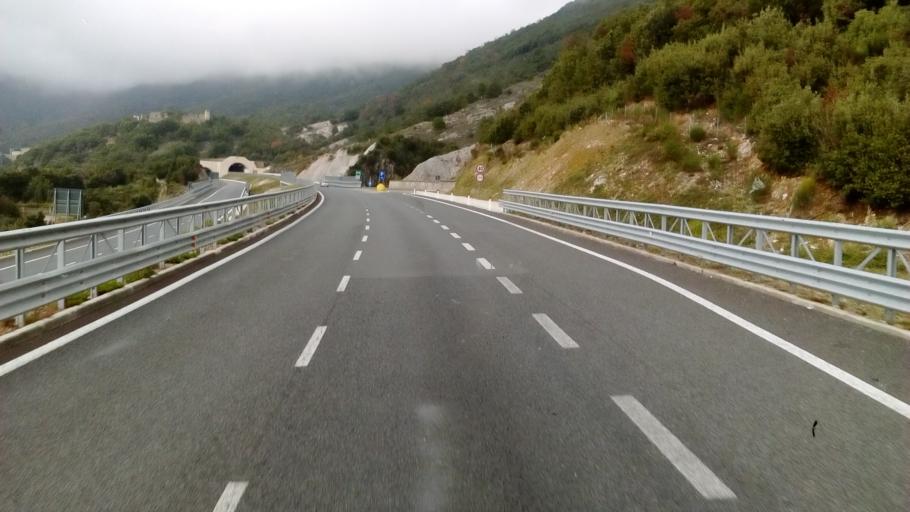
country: IT
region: Calabria
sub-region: Provincia di Cosenza
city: Morano Calabro
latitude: 39.8849
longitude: 16.1588
